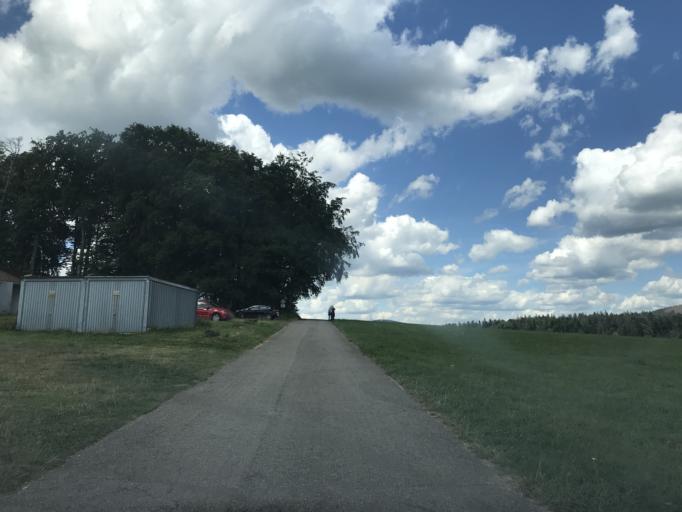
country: DE
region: Baden-Wuerttemberg
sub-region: Freiburg Region
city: Wehr
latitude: 47.6343
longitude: 7.9421
